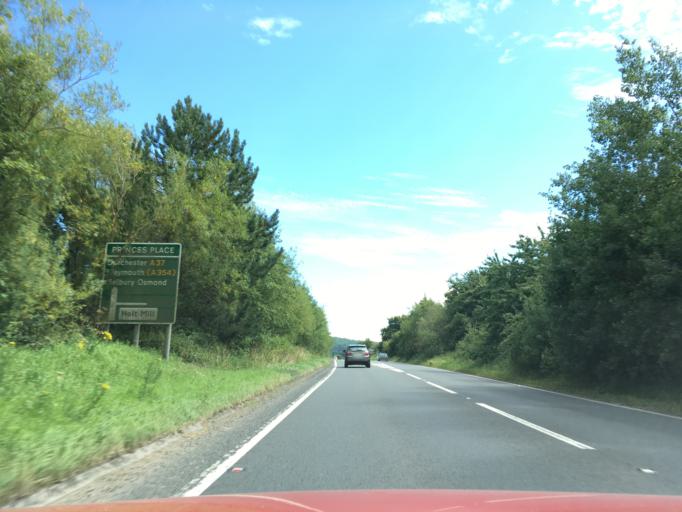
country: GB
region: England
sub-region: Somerset
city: Yeovil
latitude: 50.8823
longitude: -2.6049
